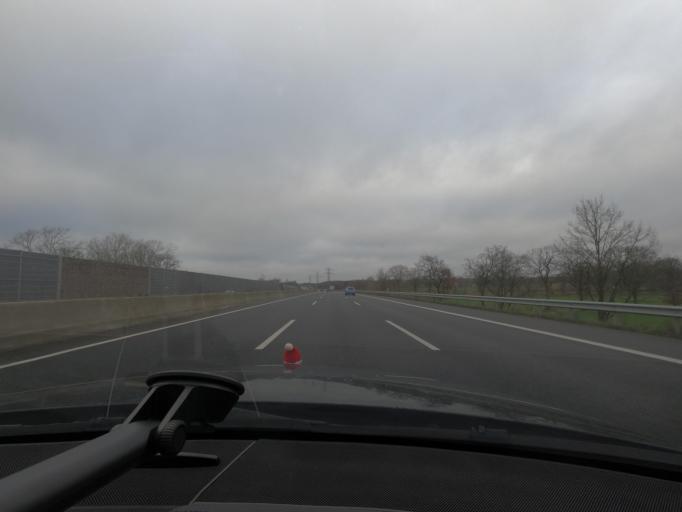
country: DE
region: Schleswig-Holstein
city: Ellerau
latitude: 53.7617
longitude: 9.9493
